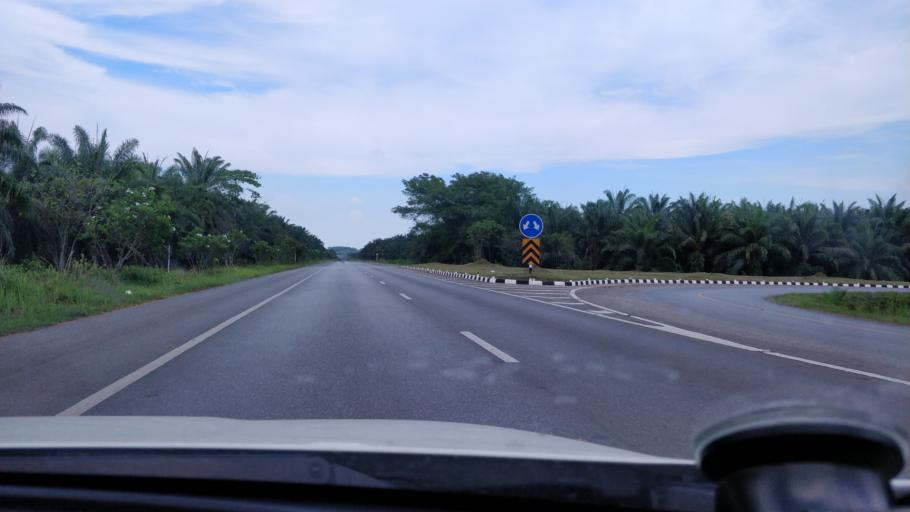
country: TH
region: Krabi
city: Plai Phraya
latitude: 8.6056
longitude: 98.9720
